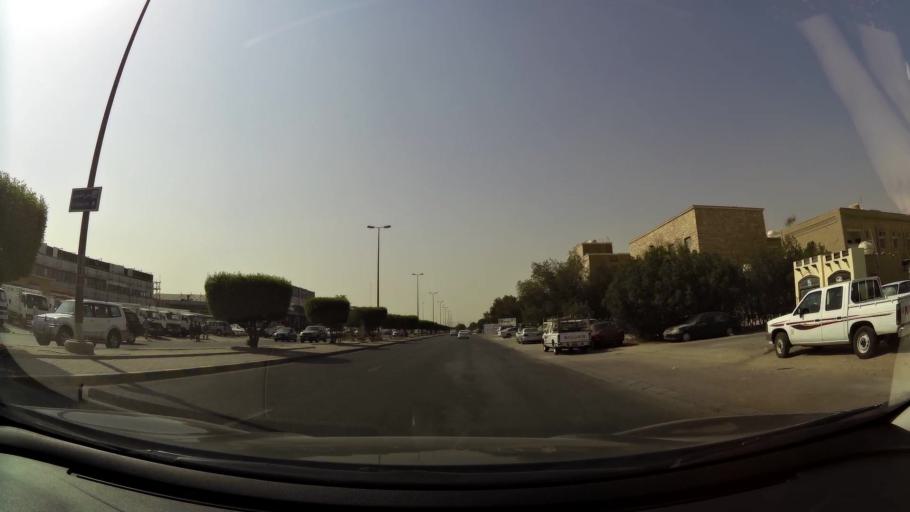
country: KW
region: Al Ahmadi
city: Al Fahahil
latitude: 29.0740
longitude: 48.1170
